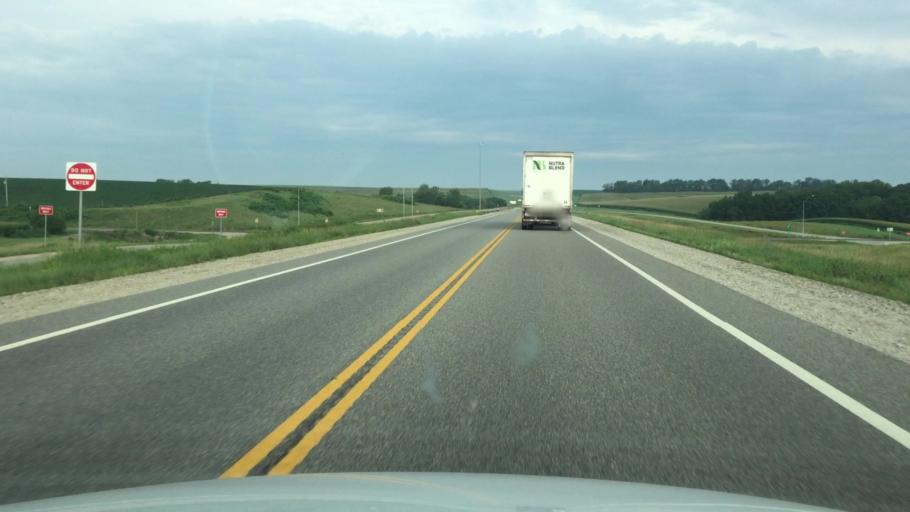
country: US
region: Kansas
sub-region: Doniphan County
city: Highland
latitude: 39.8394
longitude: -95.2624
